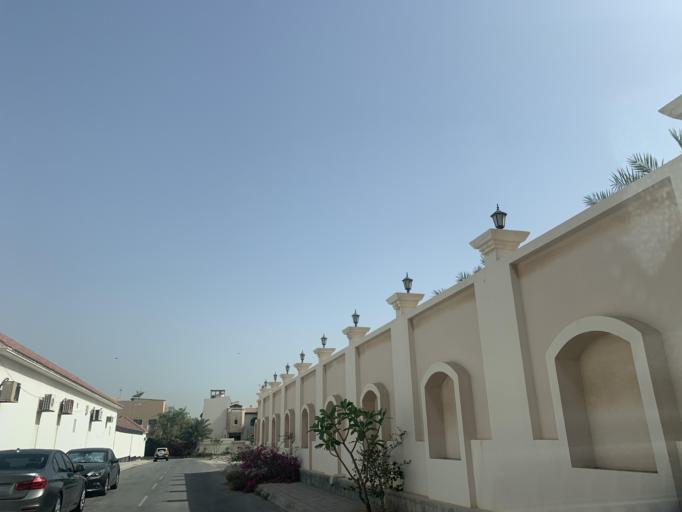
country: BH
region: Northern
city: Madinat `Isa
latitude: 26.1488
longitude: 50.5325
